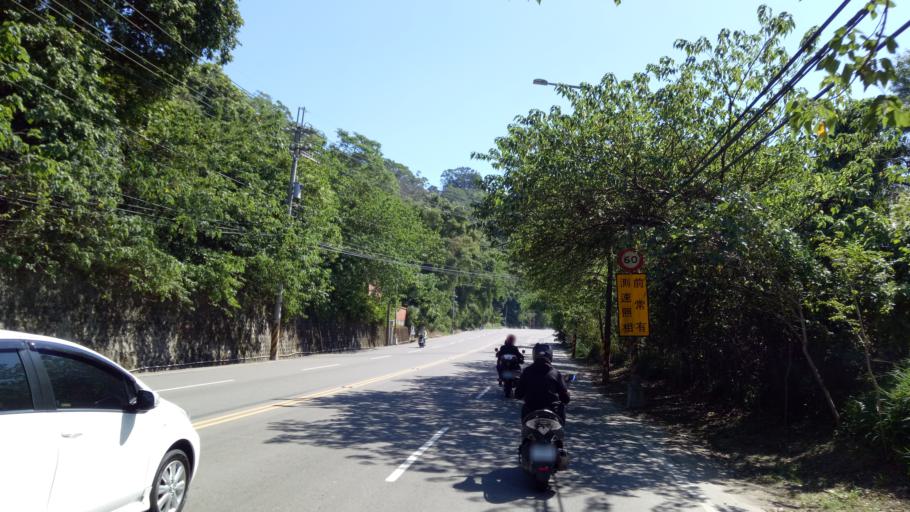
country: TW
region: Taiwan
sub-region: Hsinchu
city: Hsinchu
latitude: 24.6812
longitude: 120.9647
